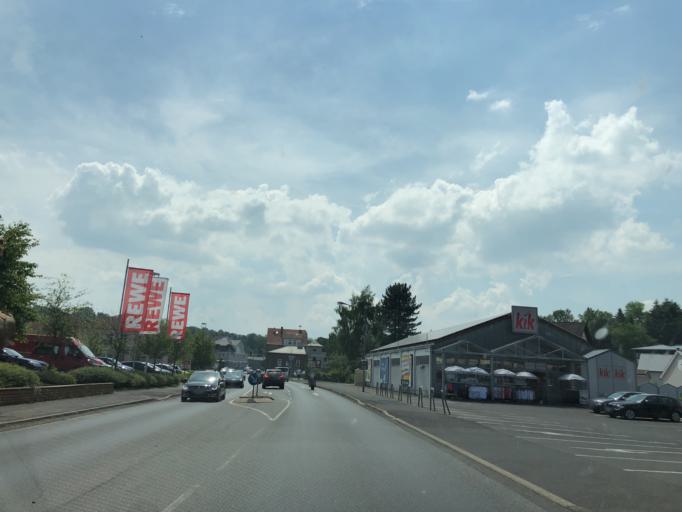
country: DE
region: Hesse
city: Schwalmstadt
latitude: 50.9141
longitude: 9.1820
